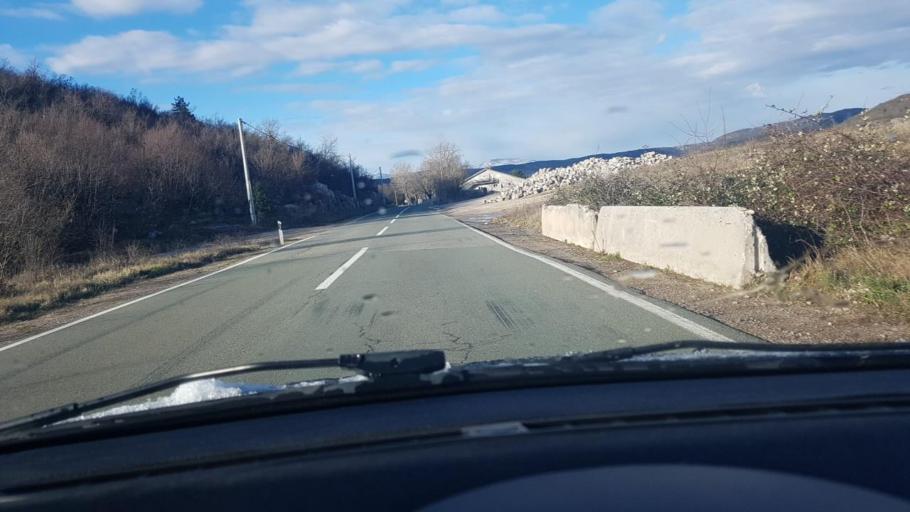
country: HR
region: Primorsko-Goranska
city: Podhum
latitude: 45.3760
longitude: 14.5048
